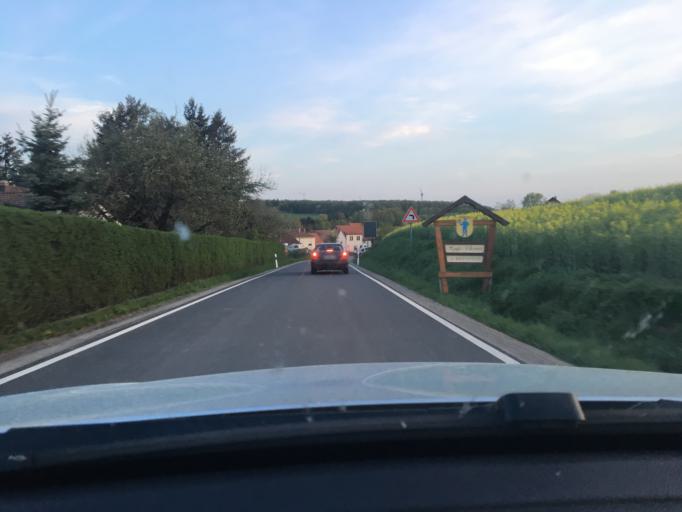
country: DE
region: Rheinland-Pfalz
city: Kriegsfeld
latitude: 49.7110
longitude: 7.9117
